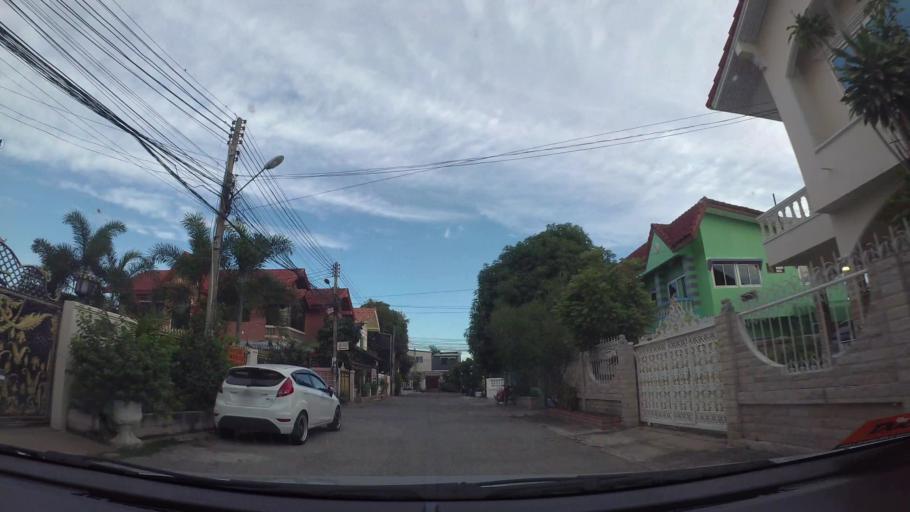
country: TH
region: Chon Buri
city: Phatthaya
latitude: 12.9132
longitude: 100.8838
